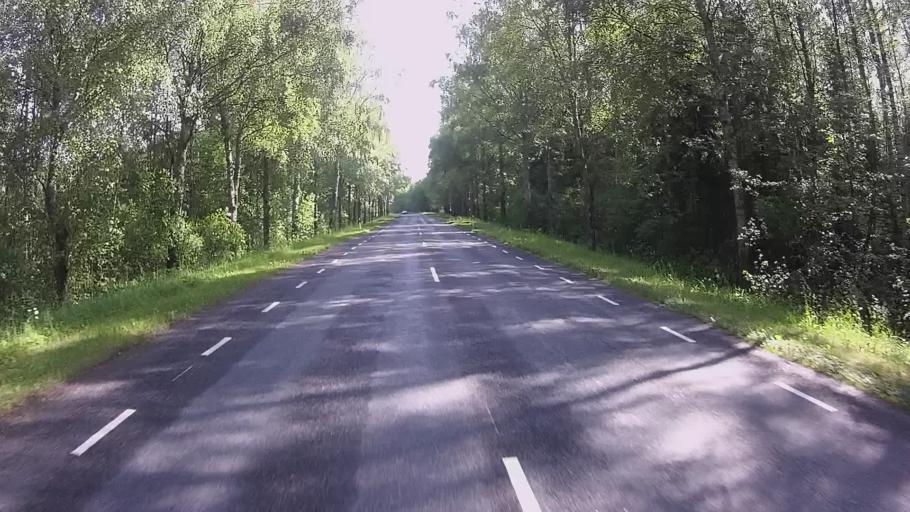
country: EE
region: Valgamaa
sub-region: Torva linn
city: Torva
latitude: 58.0738
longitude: 26.0382
